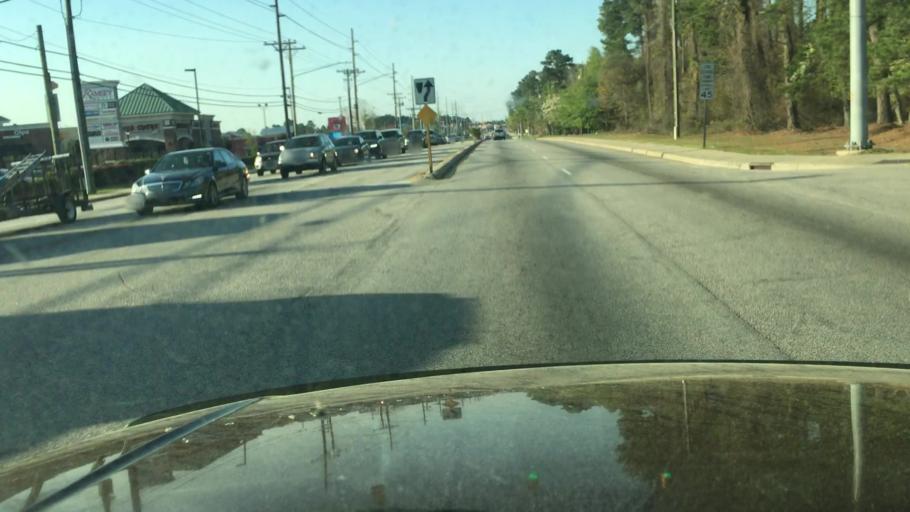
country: US
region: North Carolina
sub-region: Cumberland County
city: Fayetteville
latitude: 35.1204
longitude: -78.8796
